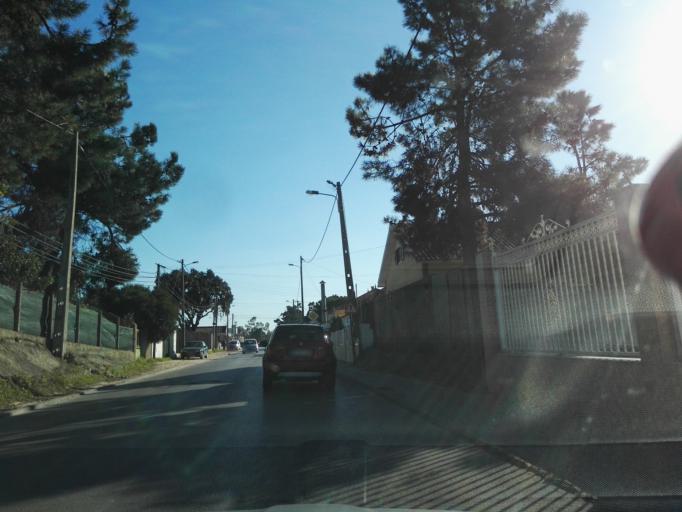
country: PT
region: Setubal
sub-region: Seixal
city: Corroios
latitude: 38.6296
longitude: -9.1457
